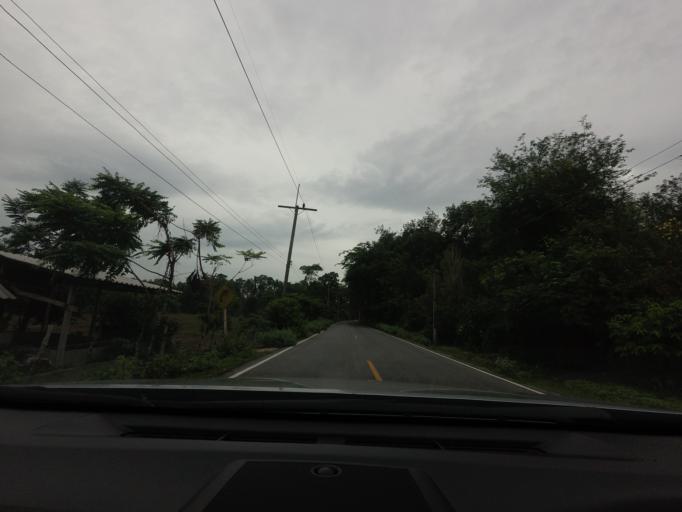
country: TH
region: Narathiwat
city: Rueso
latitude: 6.4149
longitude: 101.5257
